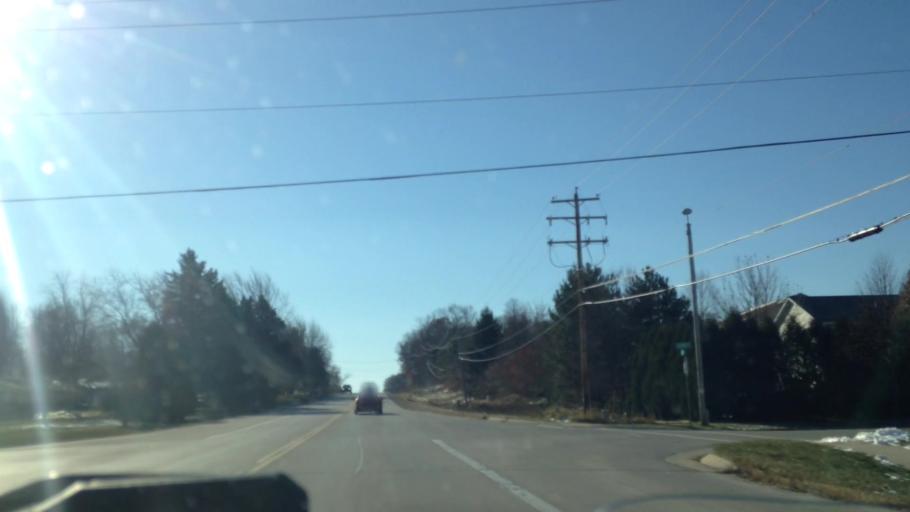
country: US
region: Wisconsin
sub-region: Washington County
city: West Bend
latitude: 43.4053
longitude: -88.1612
